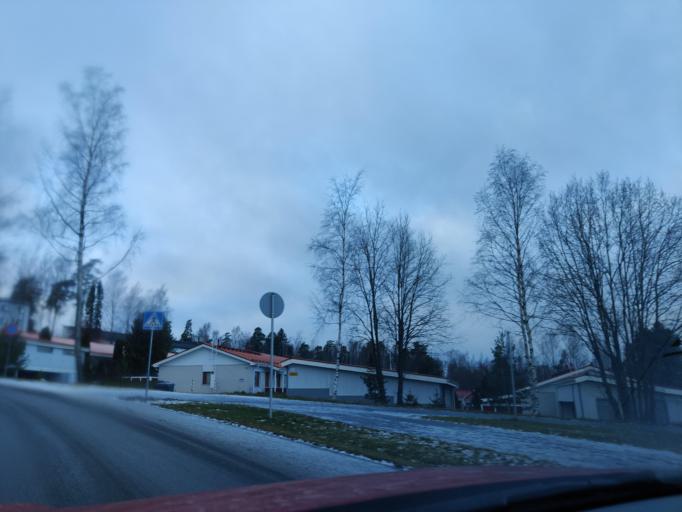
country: FI
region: Pirkanmaa
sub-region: Tampere
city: Nokia
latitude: 61.4690
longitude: 23.5019
